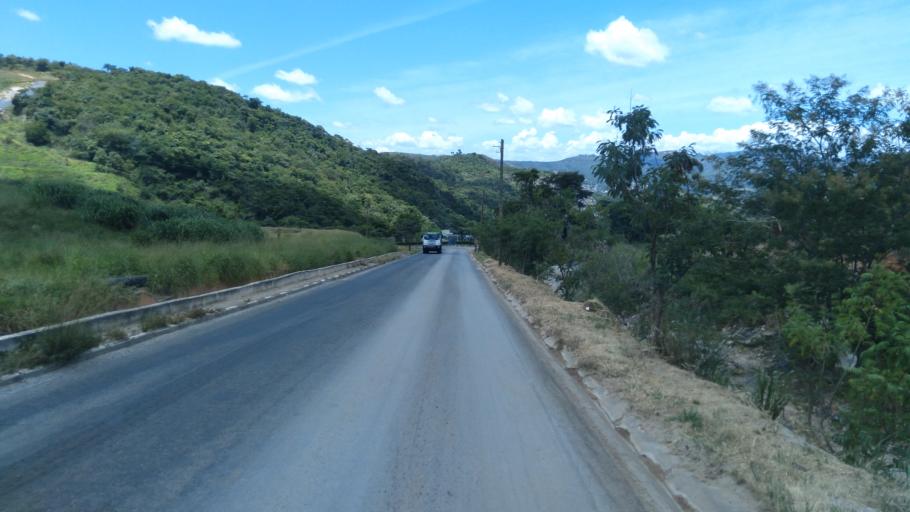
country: BR
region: Minas Gerais
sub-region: Santa Luzia
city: Santa Luzia
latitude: -19.8547
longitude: -43.8498
